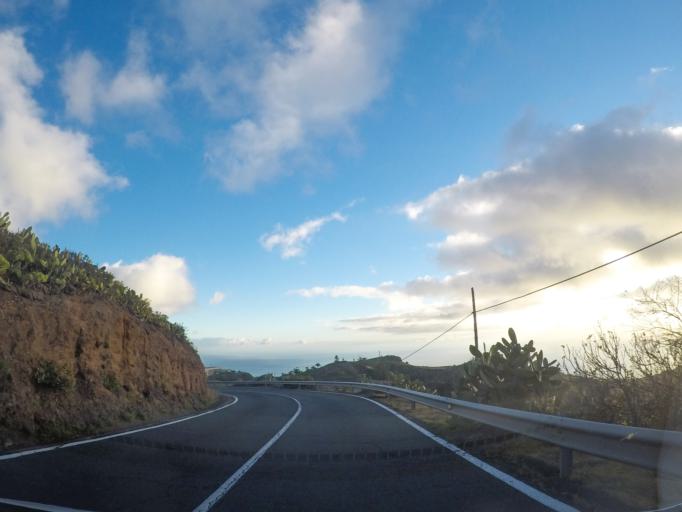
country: ES
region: Canary Islands
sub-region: Provincia de Santa Cruz de Tenerife
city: Alajero
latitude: 28.0744
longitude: -17.2389
